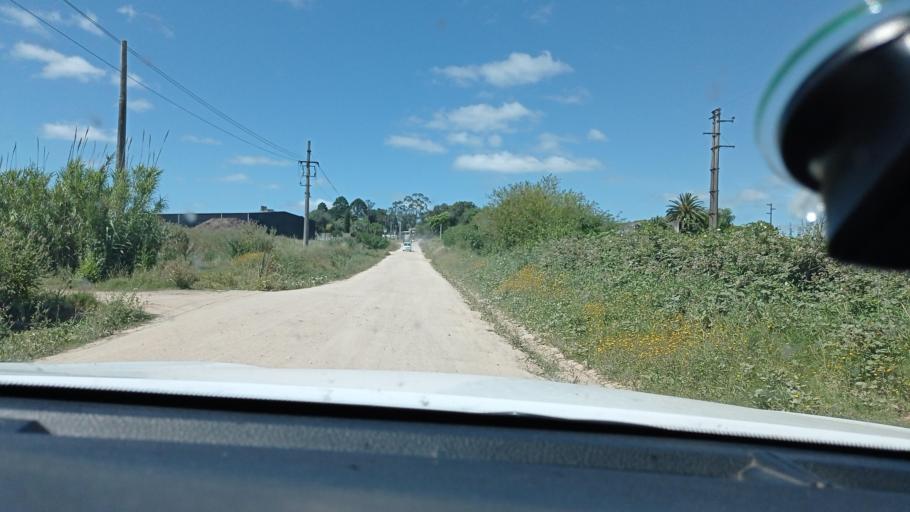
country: UY
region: Canelones
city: Pando
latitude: -34.7304
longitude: -55.9752
